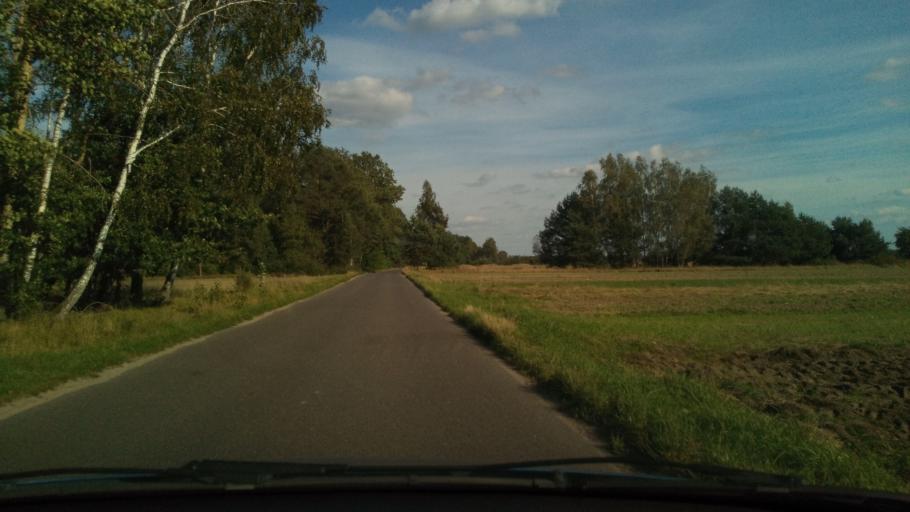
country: PL
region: Lodz Voivodeship
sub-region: Powiat piotrkowski
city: Sulejow
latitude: 51.4088
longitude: 19.8449
